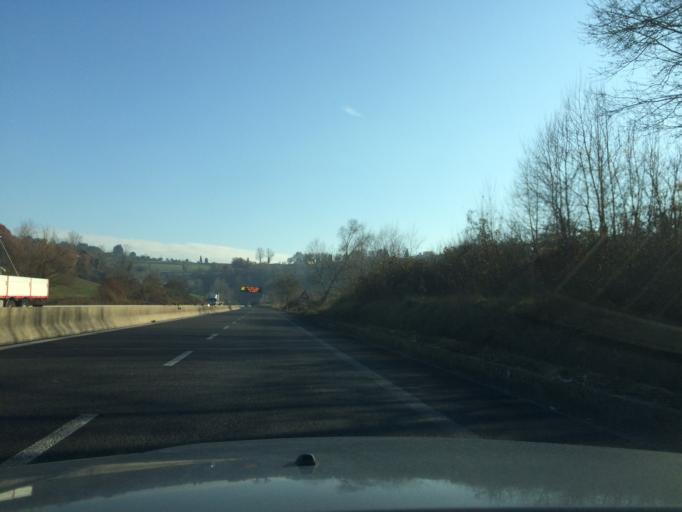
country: IT
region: Umbria
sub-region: Provincia di Perugia
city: Todi
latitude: 42.7509
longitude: 12.4665
